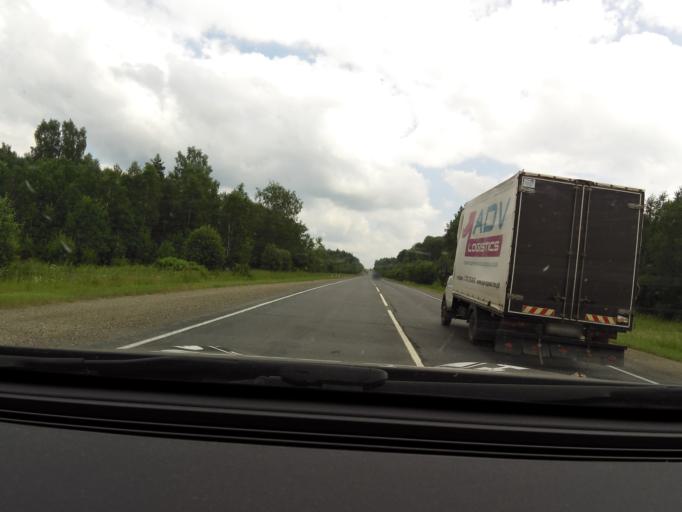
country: RU
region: Sverdlovsk
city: Achit
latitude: 56.8769
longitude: 57.6412
